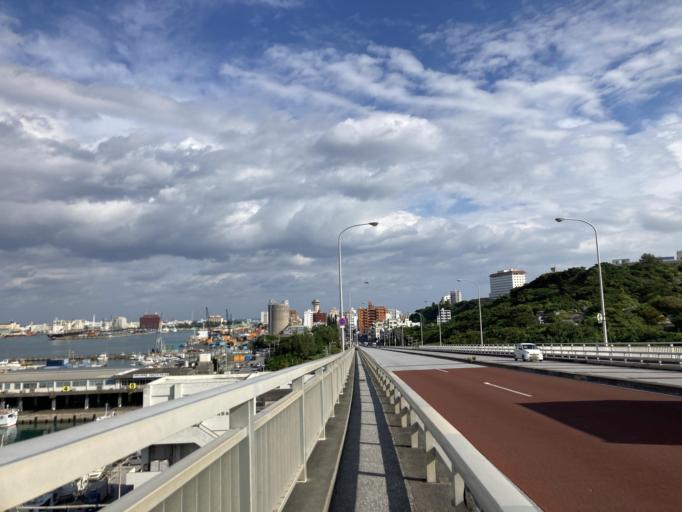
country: JP
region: Okinawa
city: Naha-shi
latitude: 26.2280
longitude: 127.6812
